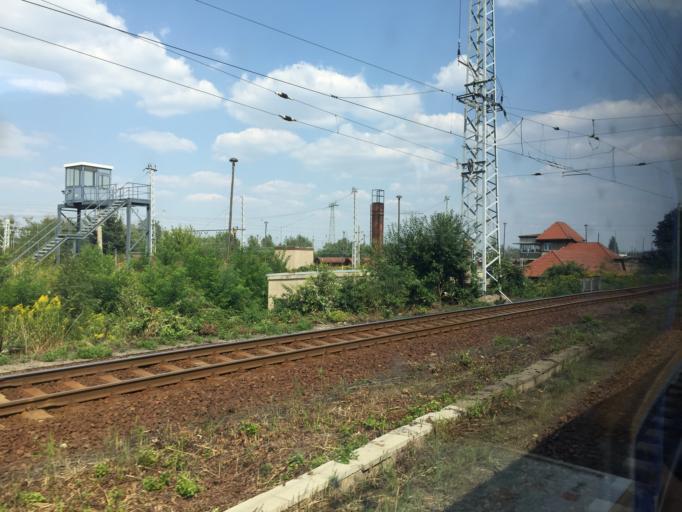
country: DE
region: Brandenburg
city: Senftenberg
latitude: 51.5322
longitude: 14.0147
